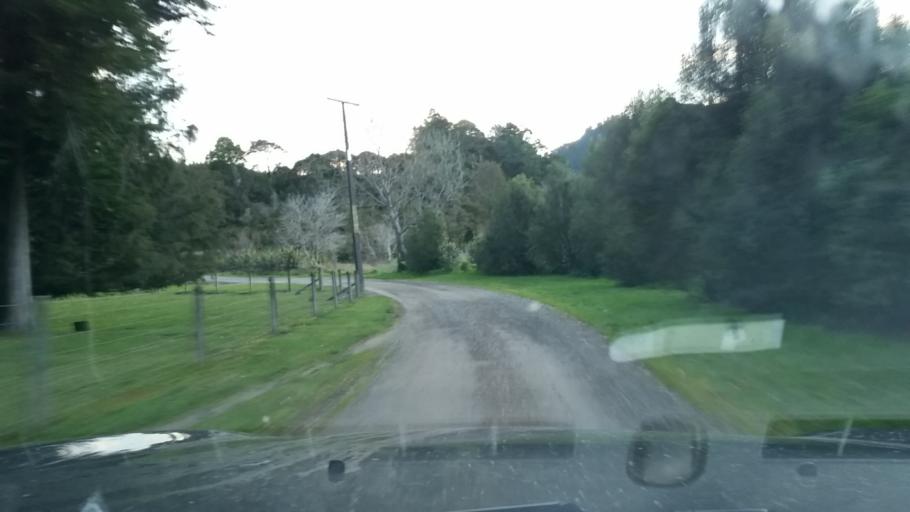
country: NZ
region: Marlborough
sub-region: Marlborough District
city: Blenheim
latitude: -41.4734
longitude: 173.7420
